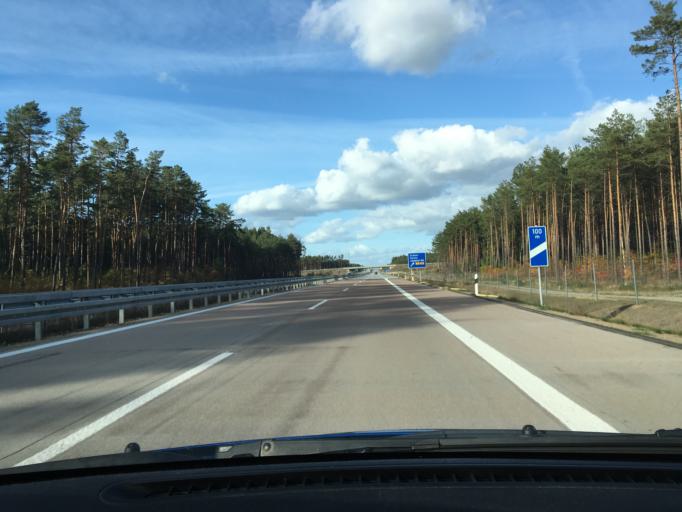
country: DE
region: Mecklenburg-Vorpommern
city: Grabow
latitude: 53.2938
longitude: 11.5273
